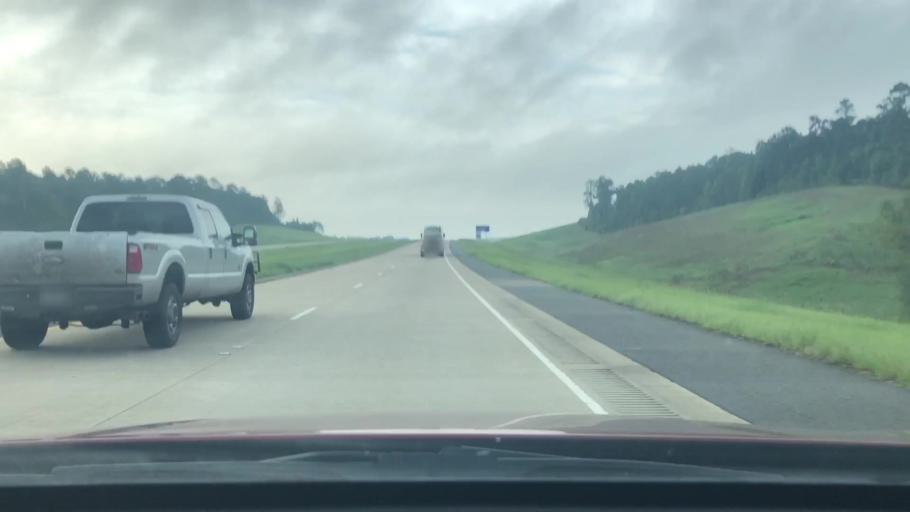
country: US
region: Louisiana
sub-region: Caddo Parish
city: Vivian
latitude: 32.9525
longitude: -93.9003
